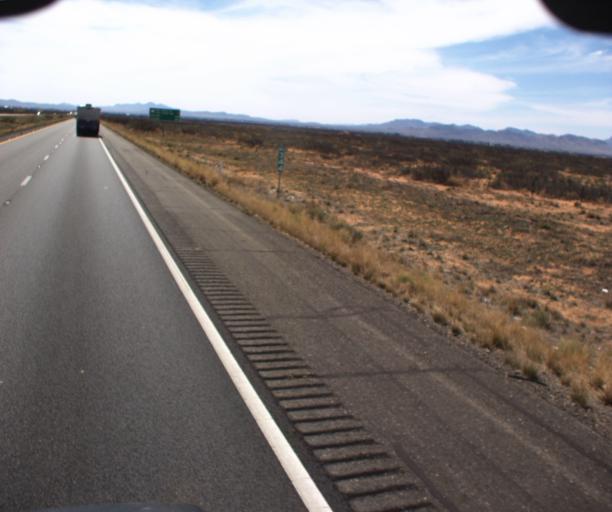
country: US
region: Arizona
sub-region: Cochise County
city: Willcox
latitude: 32.3029
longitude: -109.8029
